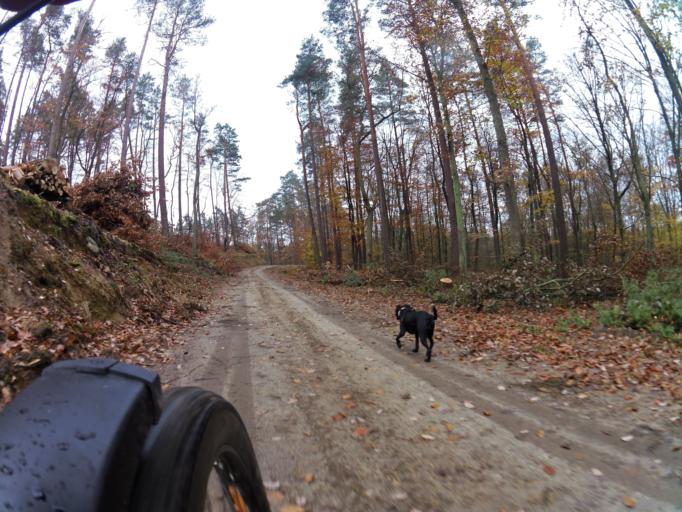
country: PL
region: Pomeranian Voivodeship
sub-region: Powiat pucki
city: Krokowa
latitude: 54.7494
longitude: 18.0907
